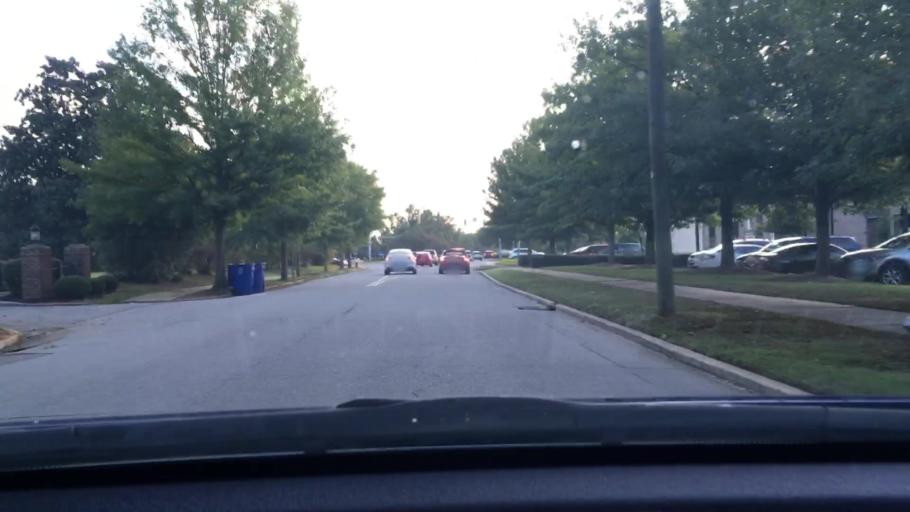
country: US
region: South Carolina
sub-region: Richland County
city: Columbia
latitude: 34.0202
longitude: -81.0380
